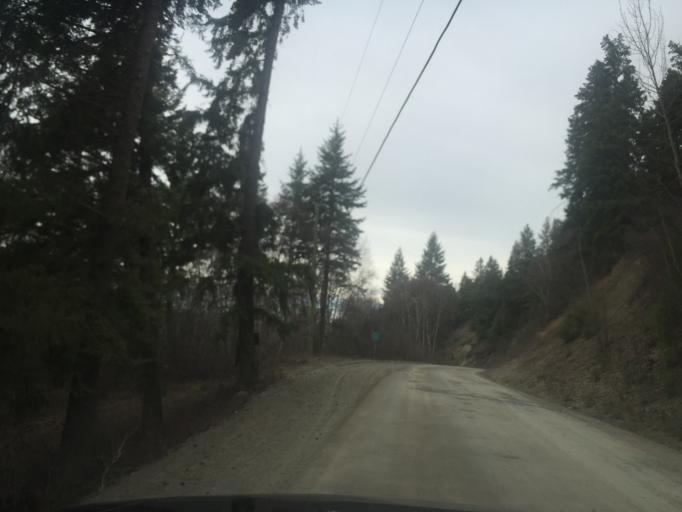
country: CA
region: British Columbia
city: Kamloops
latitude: 51.3242
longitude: -120.1479
